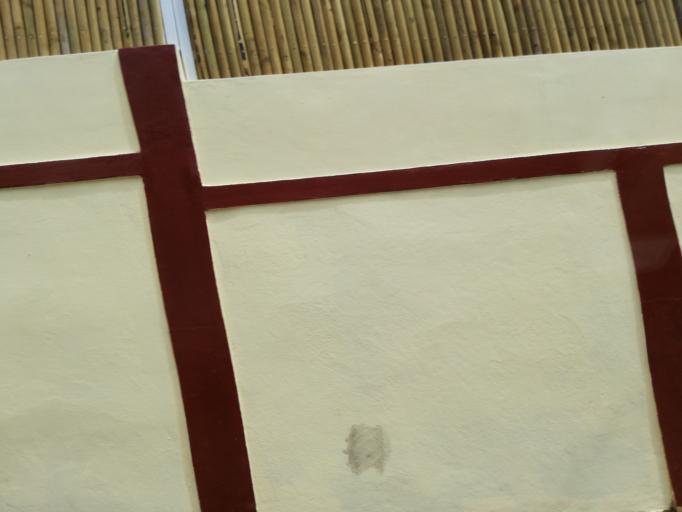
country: MU
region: Moka
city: Pailles
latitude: -20.2038
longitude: 57.4717
